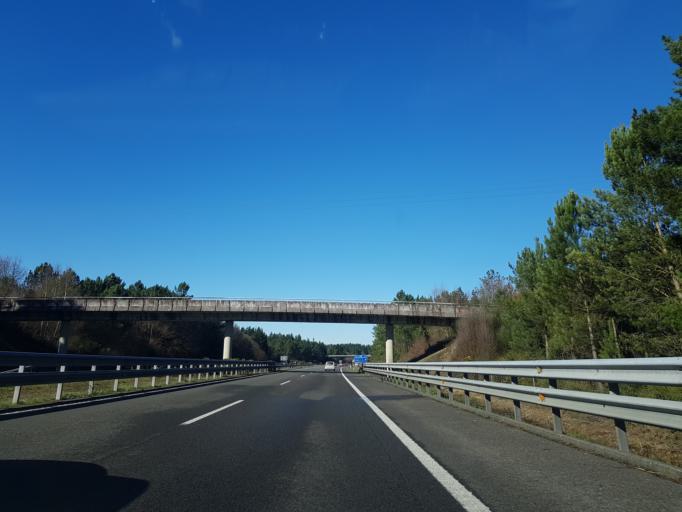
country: ES
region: Galicia
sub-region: Provincia de Lugo
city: Outeiro de Rei
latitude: 43.0974
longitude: -7.5954
